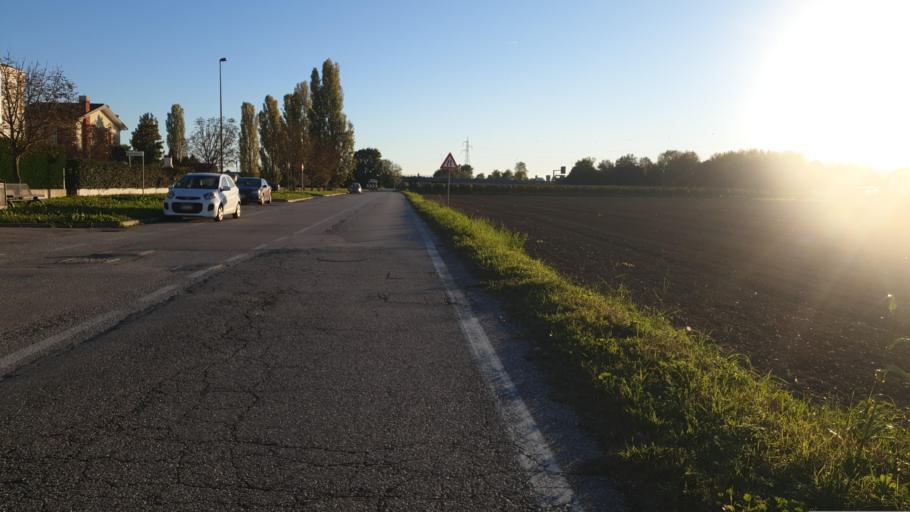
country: IT
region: Veneto
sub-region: Provincia di Venezia
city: Marano
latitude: 45.4540
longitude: 12.1006
